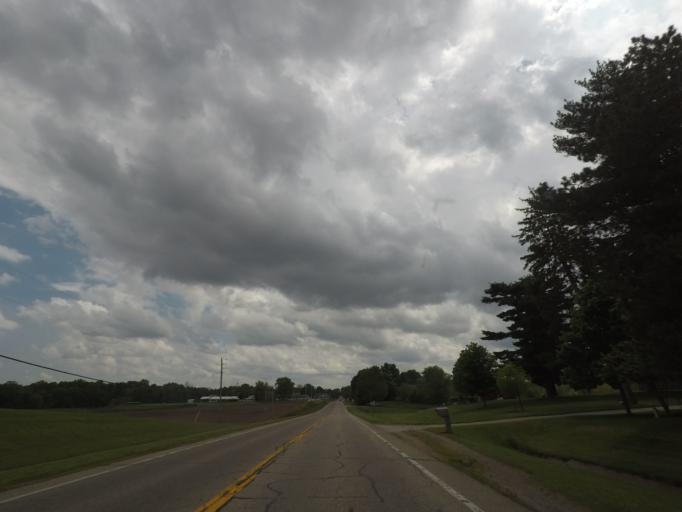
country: US
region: Illinois
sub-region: De Witt County
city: Clinton
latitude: 40.1659
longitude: -88.9605
